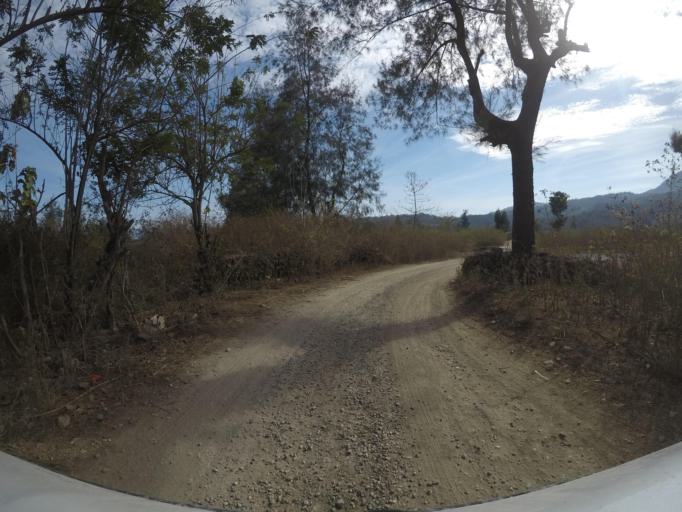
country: TL
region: Bobonaro
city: Maliana
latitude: -8.9139
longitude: 125.2149
